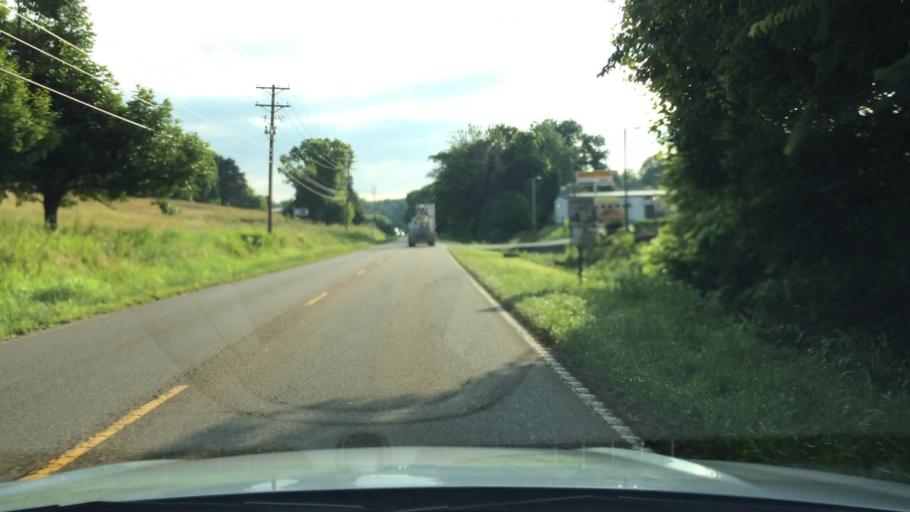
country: US
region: Tennessee
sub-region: Sevier County
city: Seymour
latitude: 35.8823
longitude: -83.7398
